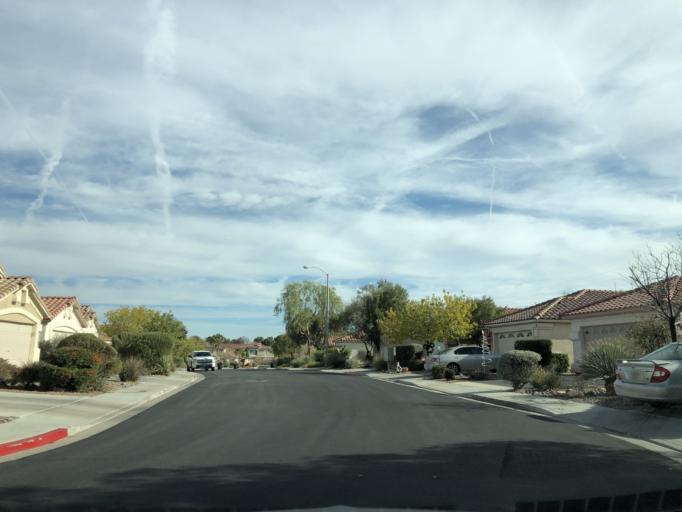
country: US
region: Nevada
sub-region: Clark County
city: Whitney
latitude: 36.0171
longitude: -115.0881
